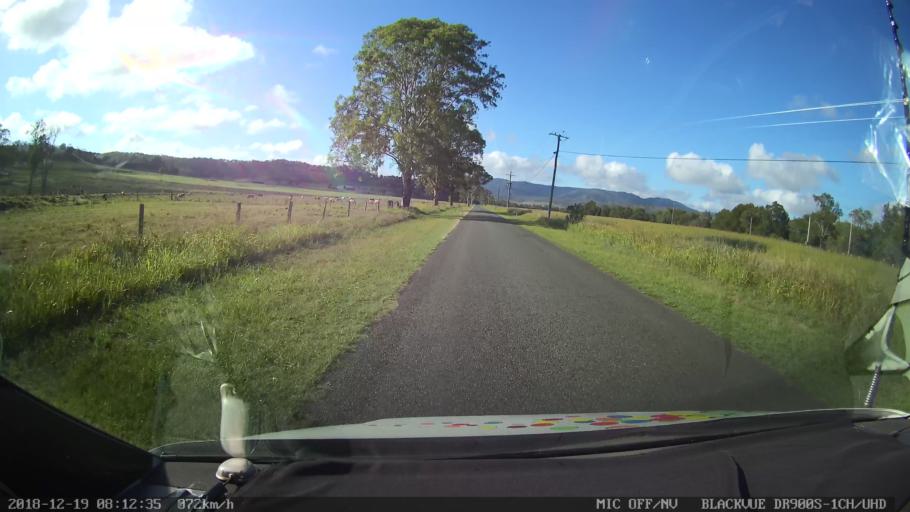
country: AU
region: Queensland
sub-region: Logan
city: Cedar Vale
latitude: -28.2288
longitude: 152.8913
